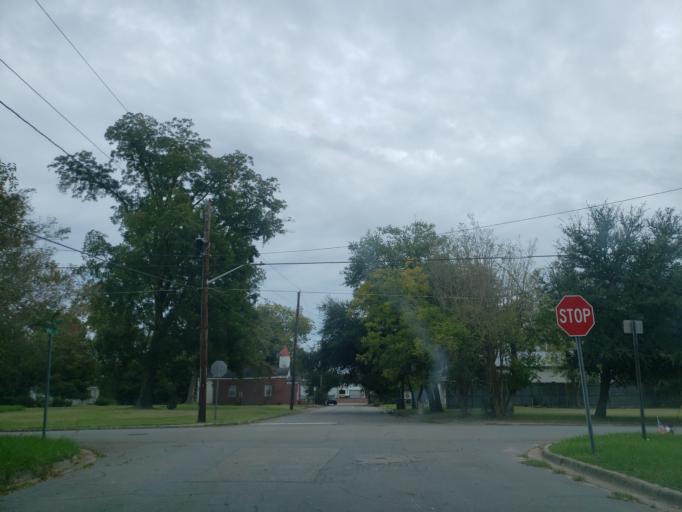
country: US
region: Georgia
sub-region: Chatham County
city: Savannah
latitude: 32.0648
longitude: -81.0836
